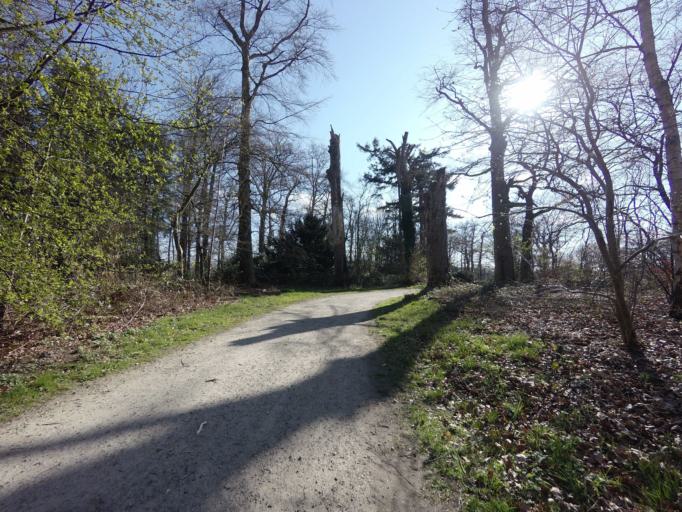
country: NL
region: North Holland
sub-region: Gemeente Wijdemeren
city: Kortenhoef
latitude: 52.2517
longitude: 5.1355
